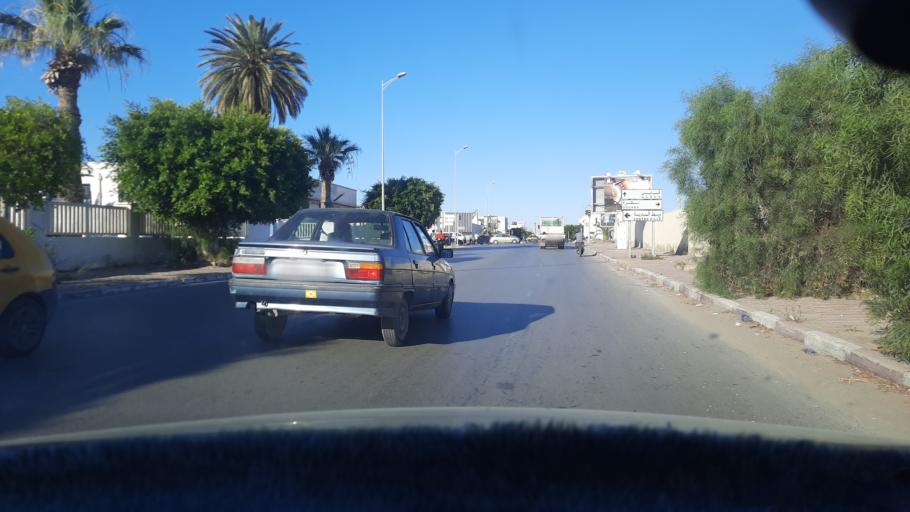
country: TN
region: Safaqis
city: Sfax
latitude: 34.7313
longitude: 10.7480
